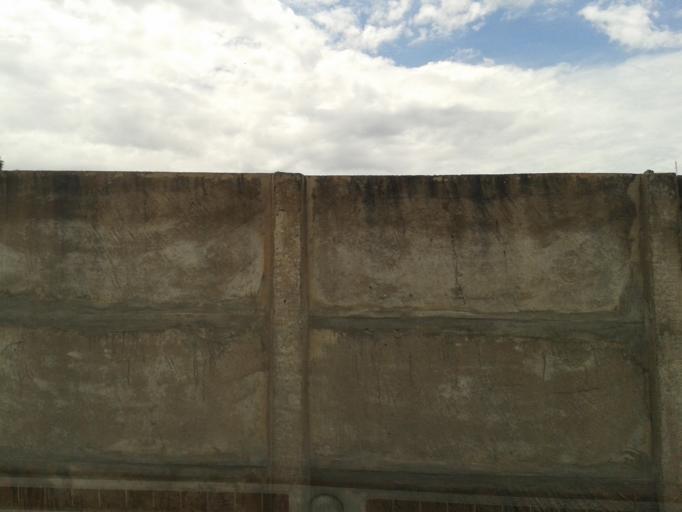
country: BR
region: Minas Gerais
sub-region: Ituiutaba
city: Ituiutaba
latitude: -18.9979
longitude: -49.4630
